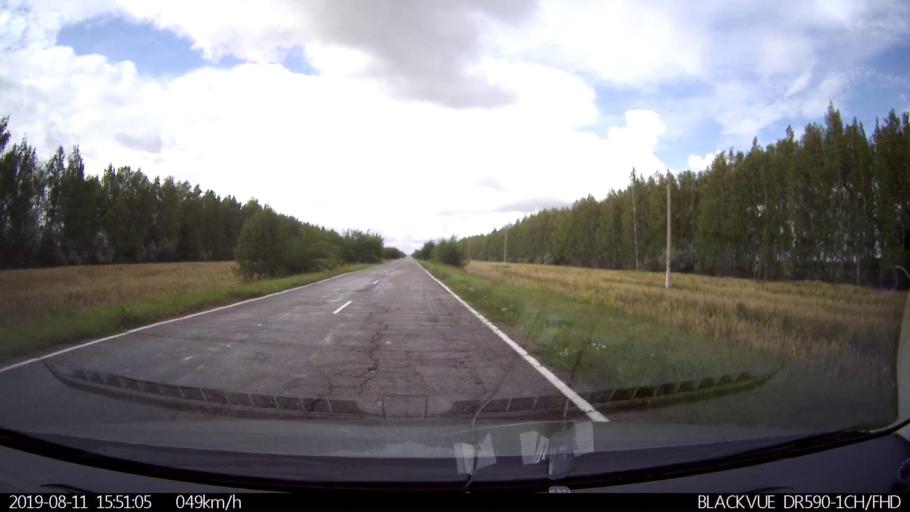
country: RU
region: Ulyanovsk
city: Ignatovka
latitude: 53.9160
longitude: 47.6559
